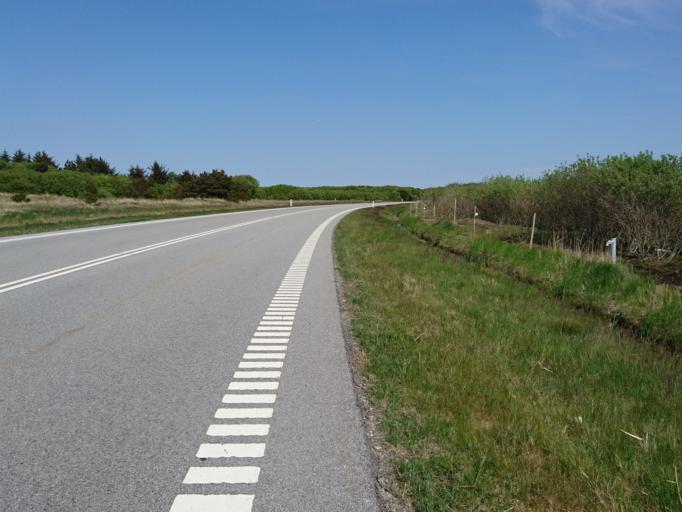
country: DK
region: North Denmark
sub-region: Frederikshavn Kommune
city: Skagen
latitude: 57.7367
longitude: 10.5810
